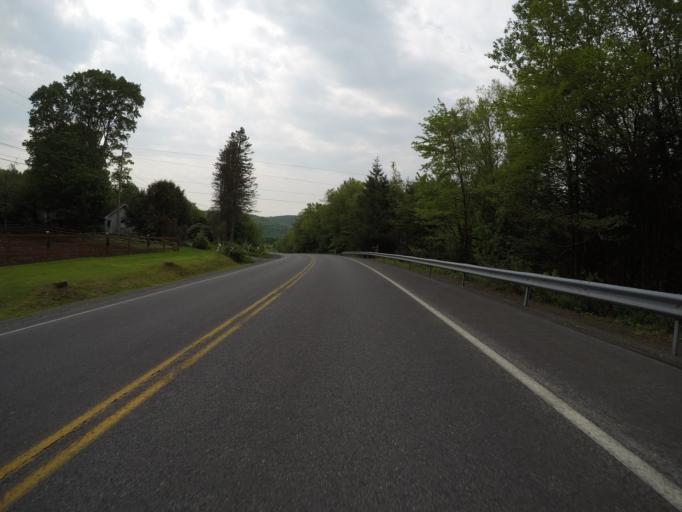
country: US
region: New York
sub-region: Sullivan County
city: Livingston Manor
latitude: 42.0324
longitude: -74.8984
